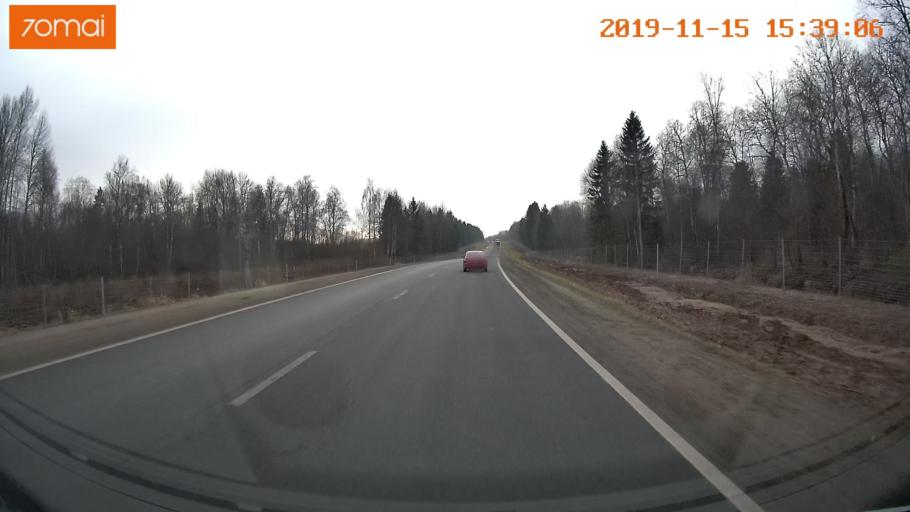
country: RU
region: Jaroslavl
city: Danilov
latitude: 58.0239
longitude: 40.0729
